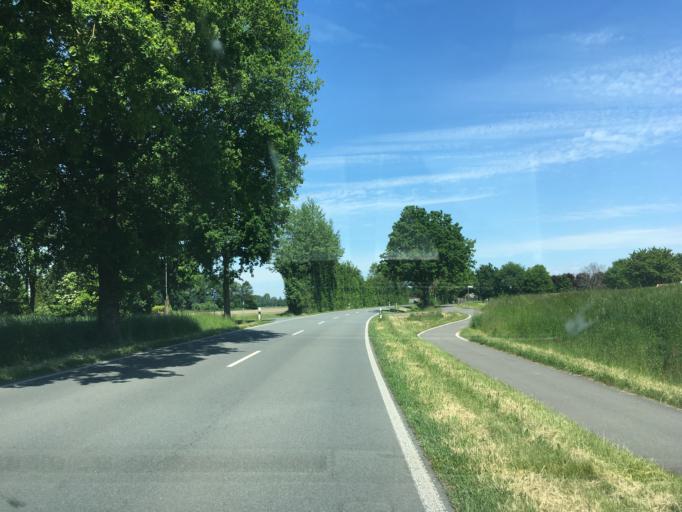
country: DE
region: North Rhine-Westphalia
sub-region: Regierungsbezirk Munster
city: Borken
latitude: 51.8925
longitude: 6.8182
